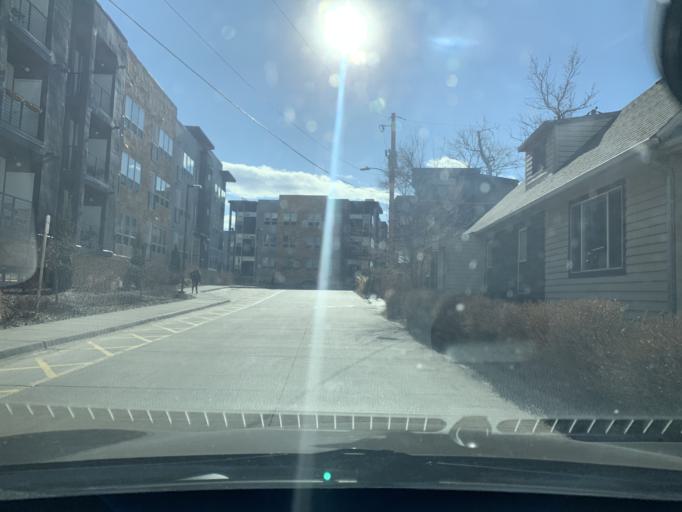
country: US
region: Colorado
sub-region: Denver County
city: Denver
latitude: 39.7511
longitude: -105.0184
